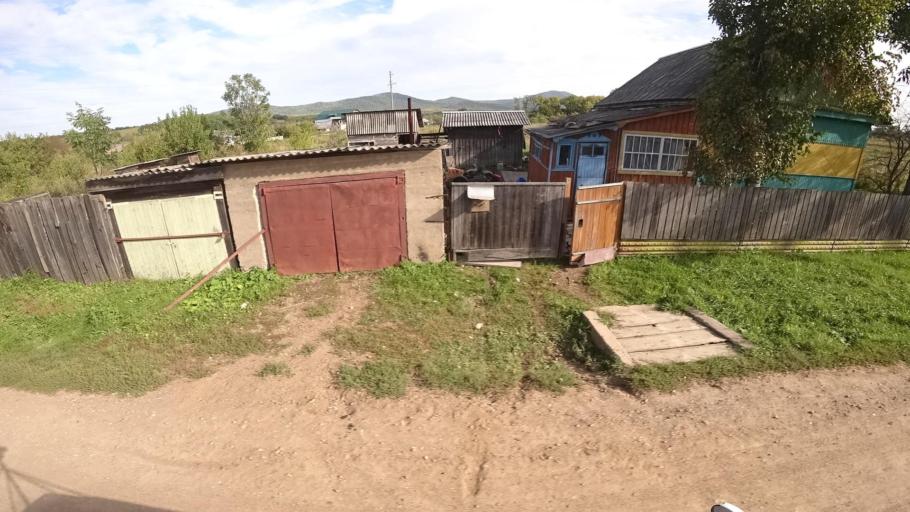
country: RU
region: Primorskiy
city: Dostoyevka
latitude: 44.3027
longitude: 133.4606
